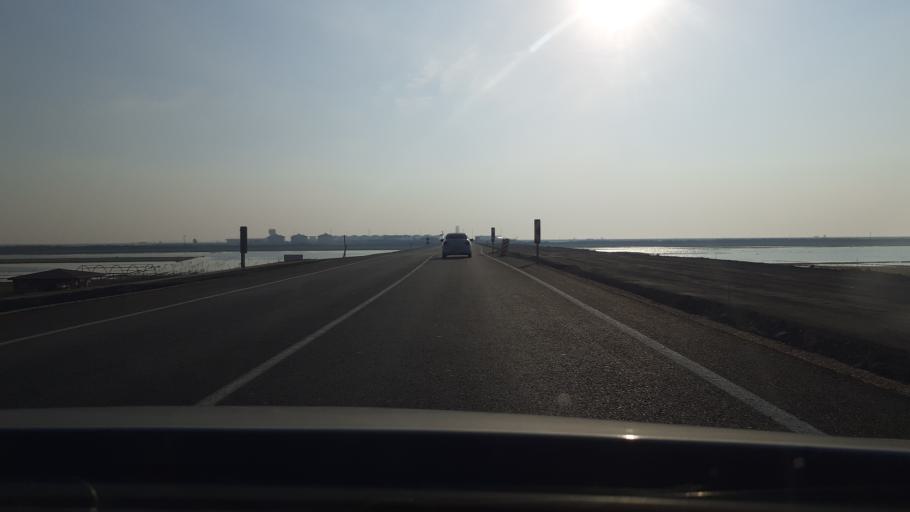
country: TR
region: Hatay
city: Serinyol
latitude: 36.3669
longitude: 36.2652
